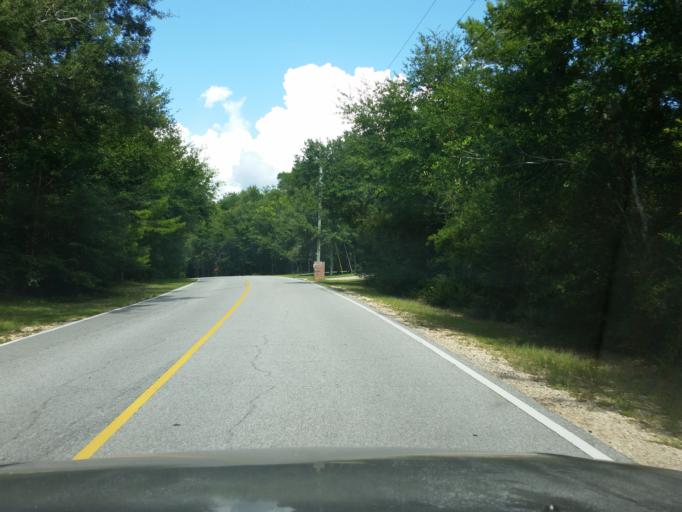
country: US
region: Alabama
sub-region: Baldwin County
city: Orange Beach
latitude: 30.3160
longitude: -87.4810
